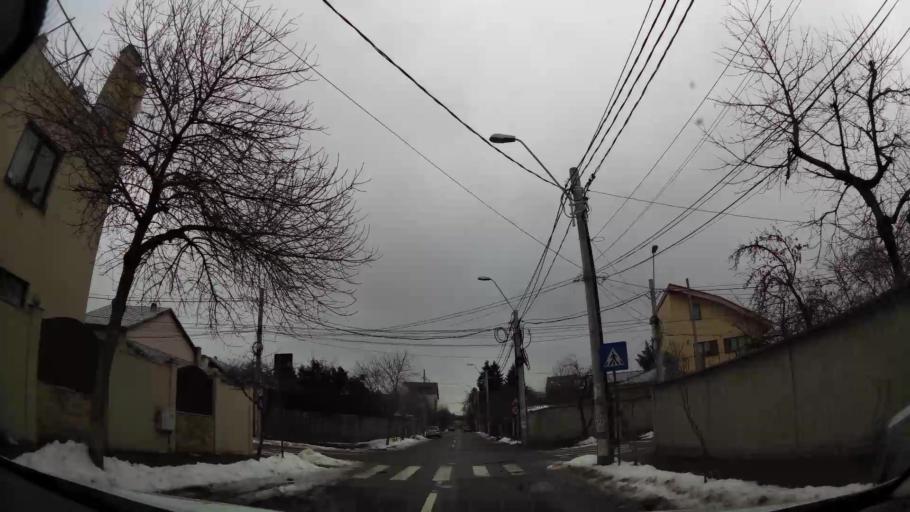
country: RO
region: Ilfov
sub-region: Comuna Chiajna
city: Rosu
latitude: 44.4884
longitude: 26.0289
